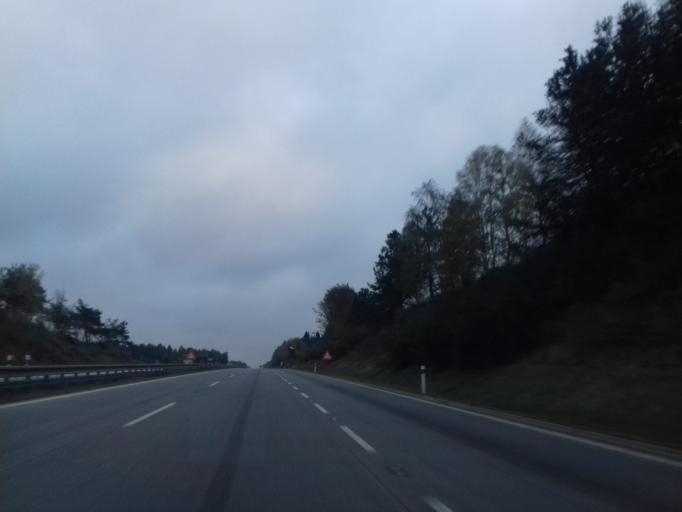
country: CZ
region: Central Bohemia
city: Cechtice
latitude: 49.6467
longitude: 15.1247
